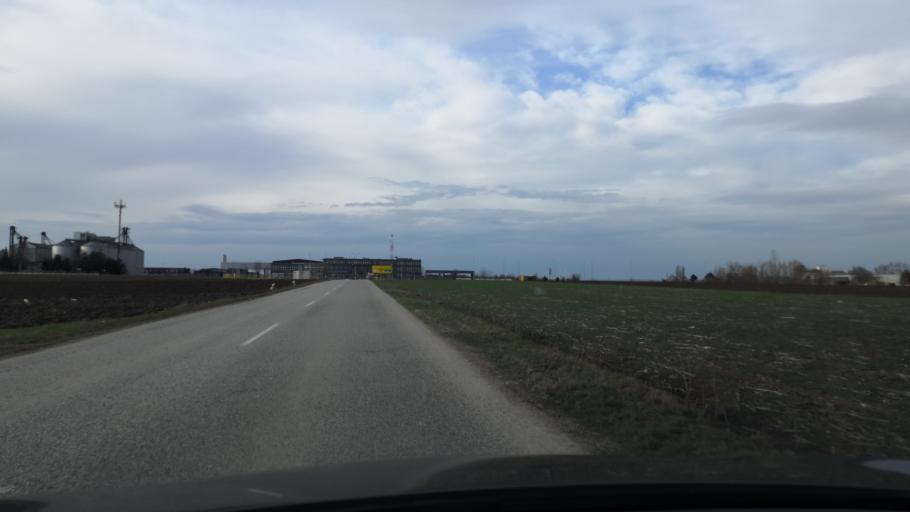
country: RS
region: Autonomna Pokrajina Vojvodina
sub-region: Sremski Okrug
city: Ingija
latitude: 45.0528
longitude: 20.1051
